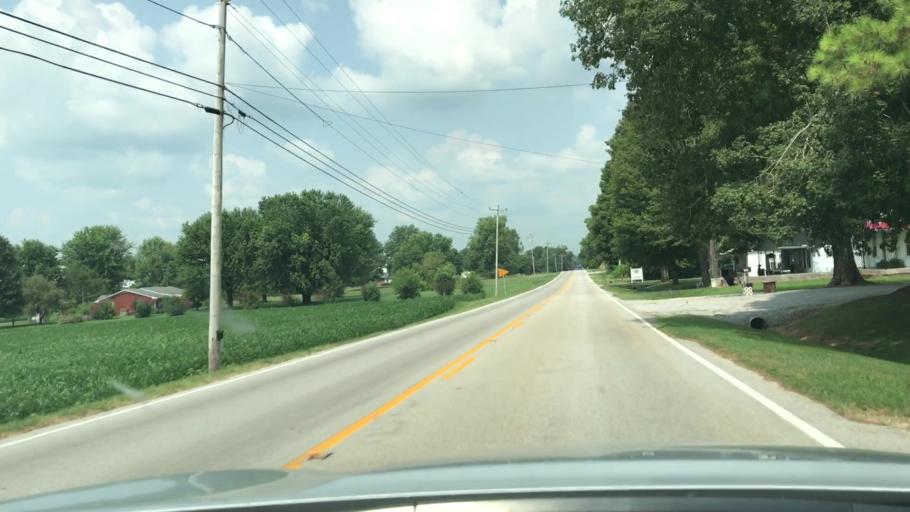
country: US
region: Kentucky
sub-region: Todd County
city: Elkton
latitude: 36.8055
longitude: -87.1282
